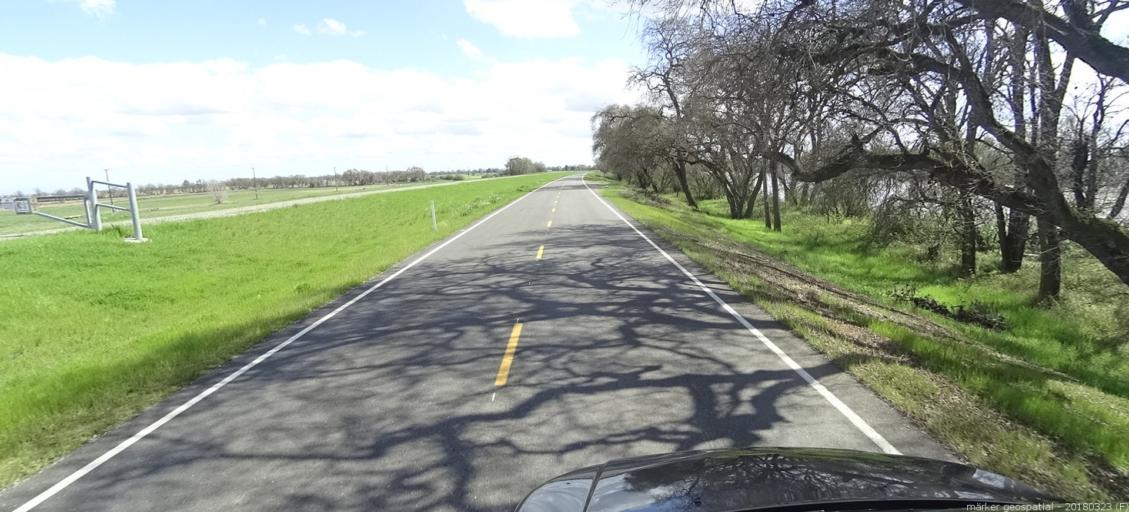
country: US
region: California
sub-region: Yolo County
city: West Sacramento
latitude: 38.6597
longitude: -121.6059
